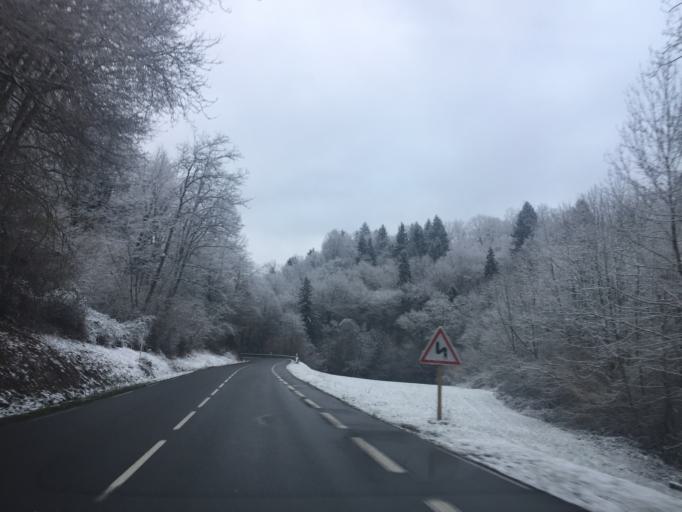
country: FR
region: Rhone-Alpes
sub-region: Departement de la Savoie
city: Gresy-sur-Aix
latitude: 45.7361
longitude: 5.9664
